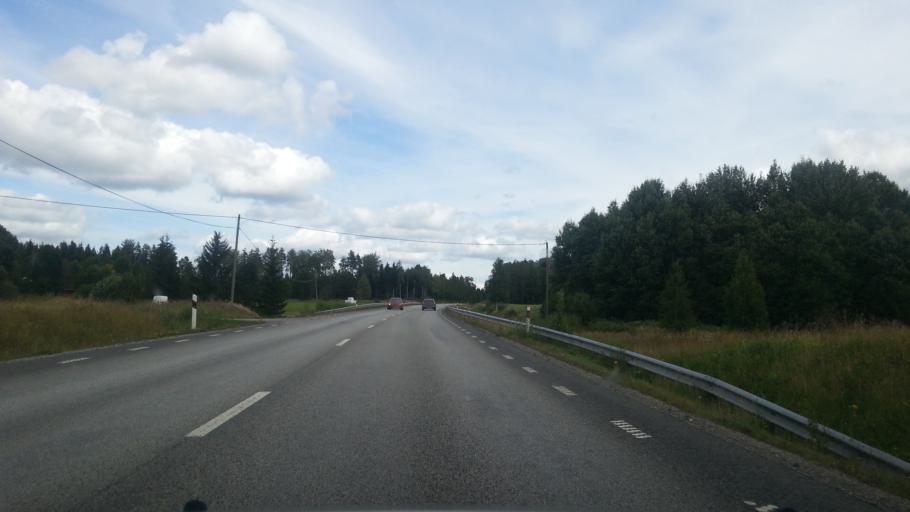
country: SE
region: OErebro
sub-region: Lindesbergs Kommun
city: Lindesberg
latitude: 59.6611
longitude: 15.2566
